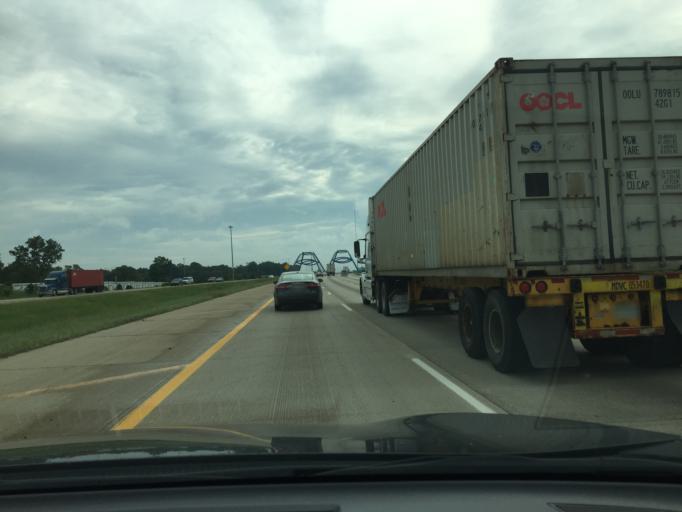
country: US
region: Michigan
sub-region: Wayne County
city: Taylor
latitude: 42.2644
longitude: -83.2770
